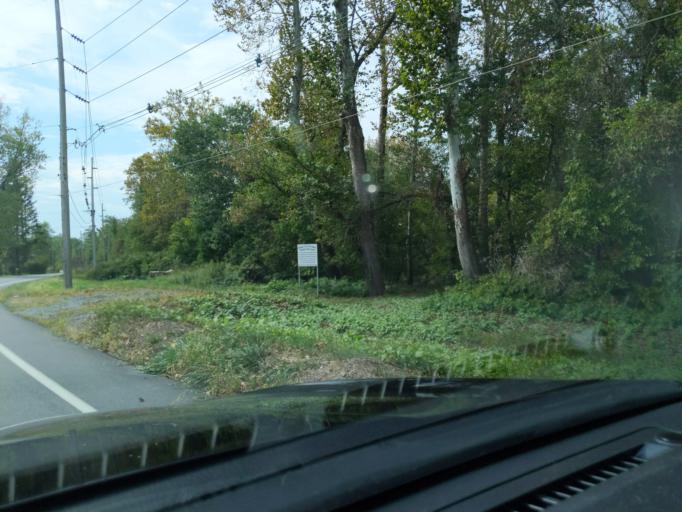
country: US
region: Pennsylvania
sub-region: Blair County
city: Hollidaysburg
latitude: 40.4409
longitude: -78.3546
